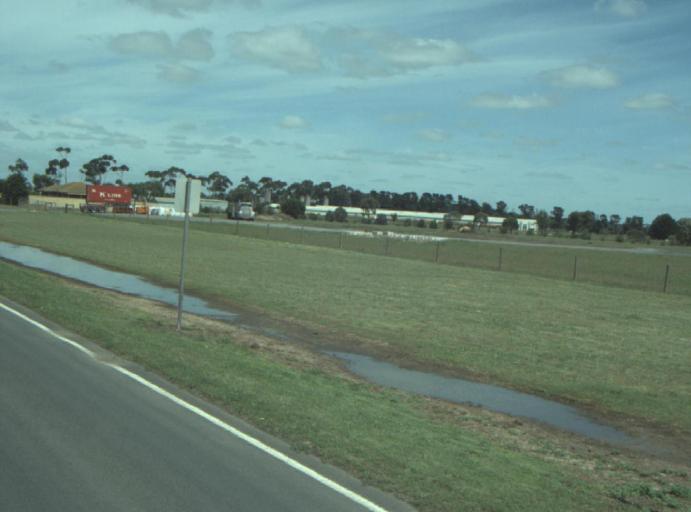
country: AU
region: Victoria
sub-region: Greater Geelong
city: Lara
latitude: -38.0251
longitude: 144.4358
